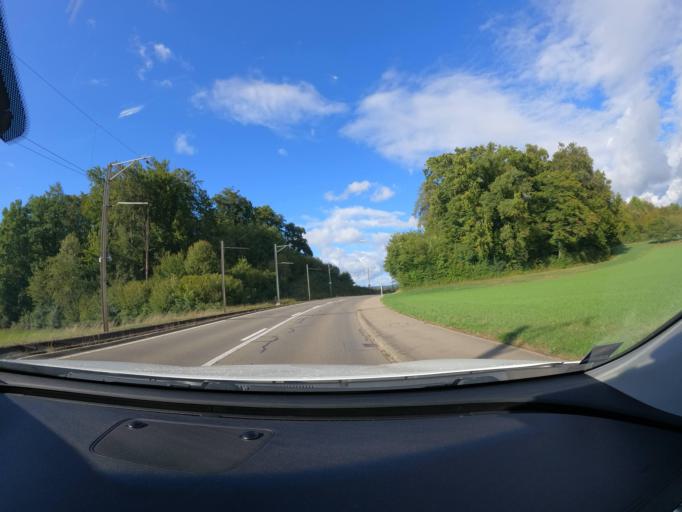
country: CH
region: Aargau
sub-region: Bezirk Lenzburg
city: Seon
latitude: 47.3590
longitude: 8.1617
